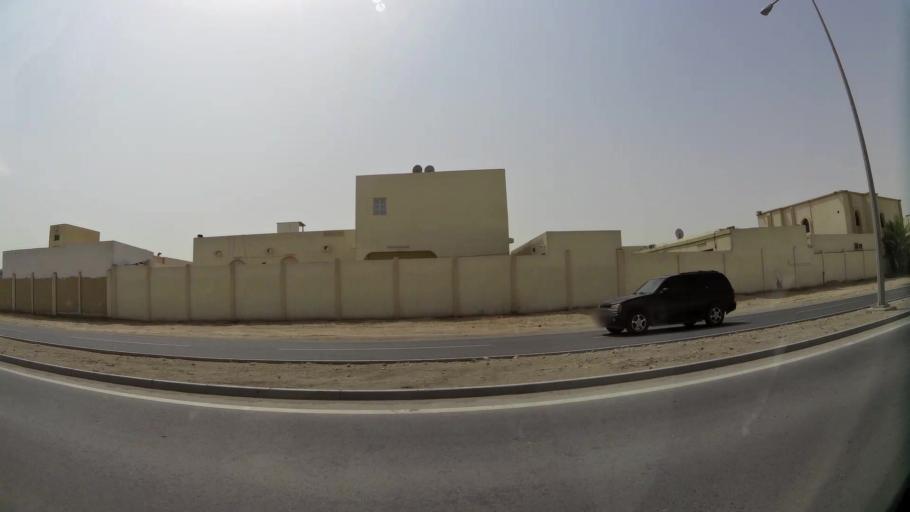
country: QA
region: Baladiyat ar Rayyan
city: Ar Rayyan
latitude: 25.2321
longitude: 51.3841
